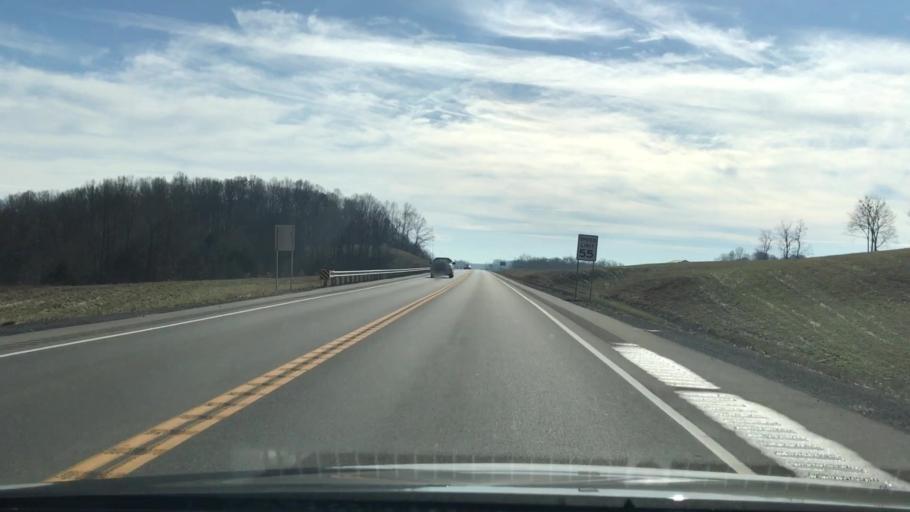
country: US
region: Kentucky
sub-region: Monroe County
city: Tompkinsville
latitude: 36.8201
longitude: -85.6885
